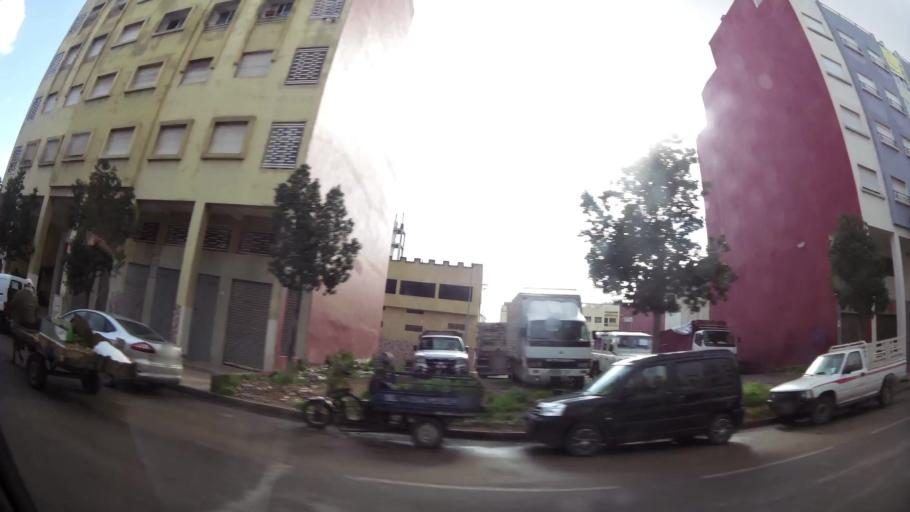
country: MA
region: Grand Casablanca
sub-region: Mediouna
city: Tit Mellil
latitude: 33.5834
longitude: -7.5248
